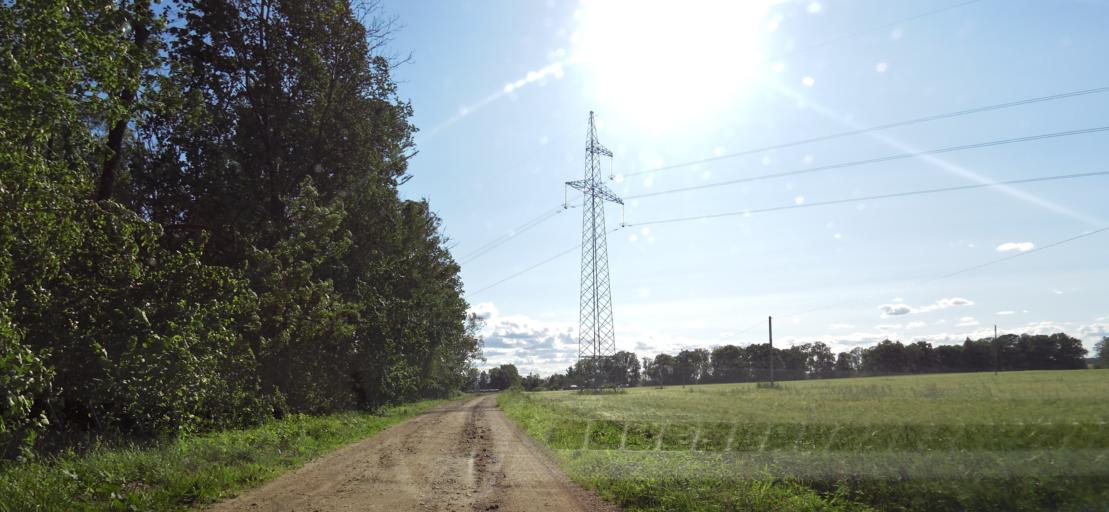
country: LT
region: Panevezys
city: Pasvalys
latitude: 56.1219
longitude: 24.4670
